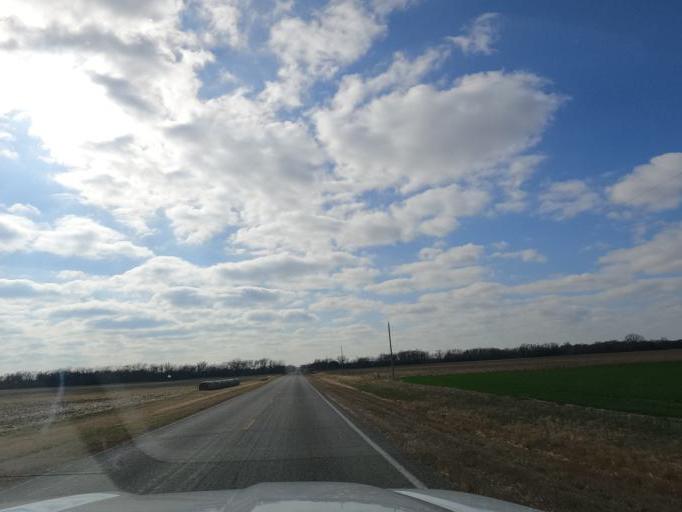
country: US
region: Kansas
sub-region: McPherson County
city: Inman
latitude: 38.2321
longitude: -97.8568
